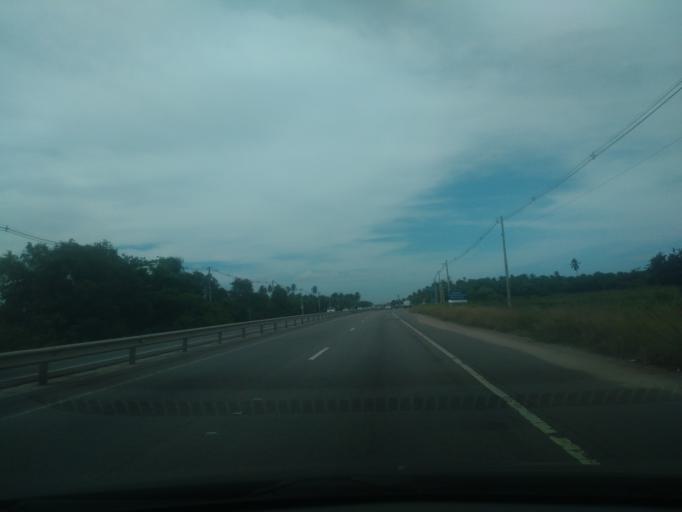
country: BR
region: Alagoas
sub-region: Marechal Deodoro
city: Marechal Deodoro
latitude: -9.7085
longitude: -35.8149
